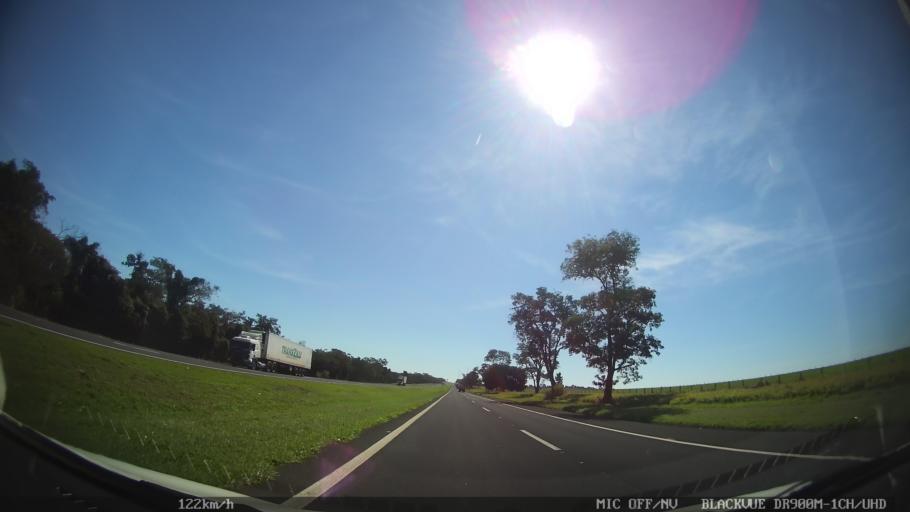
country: BR
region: Sao Paulo
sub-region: Santa Rita Do Passa Quatro
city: Santa Rita do Passa Quatro
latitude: -21.6367
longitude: -47.6125
